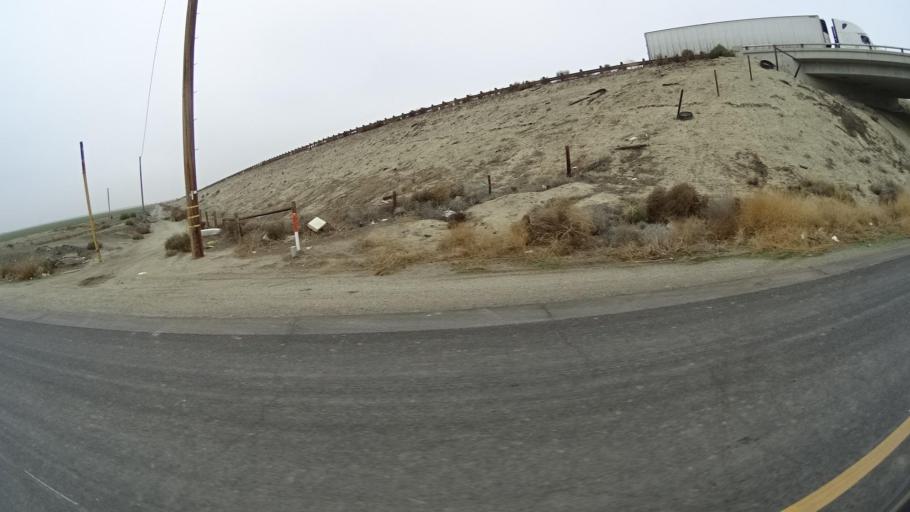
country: US
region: California
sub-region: Kern County
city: Greenfield
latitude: 35.1800
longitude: -119.1321
